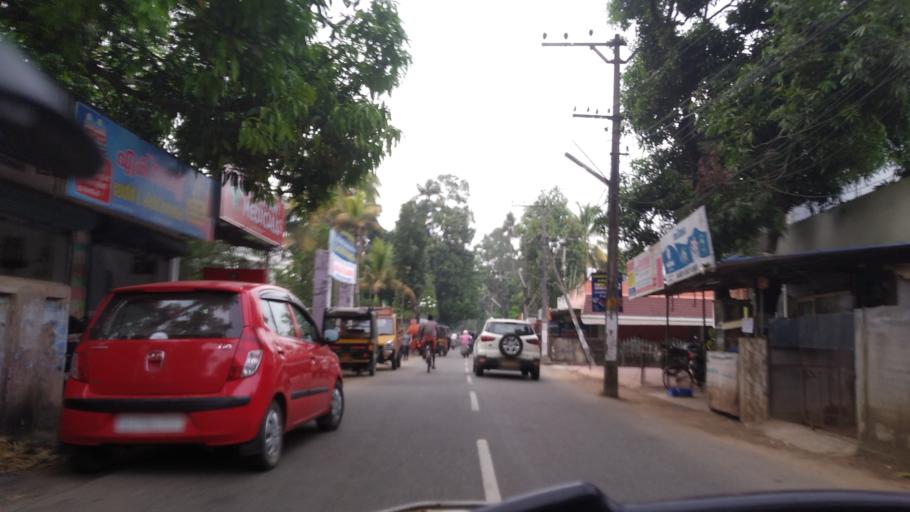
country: IN
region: Kerala
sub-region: Thrissur District
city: Kodungallur
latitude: 10.1412
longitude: 76.2178
